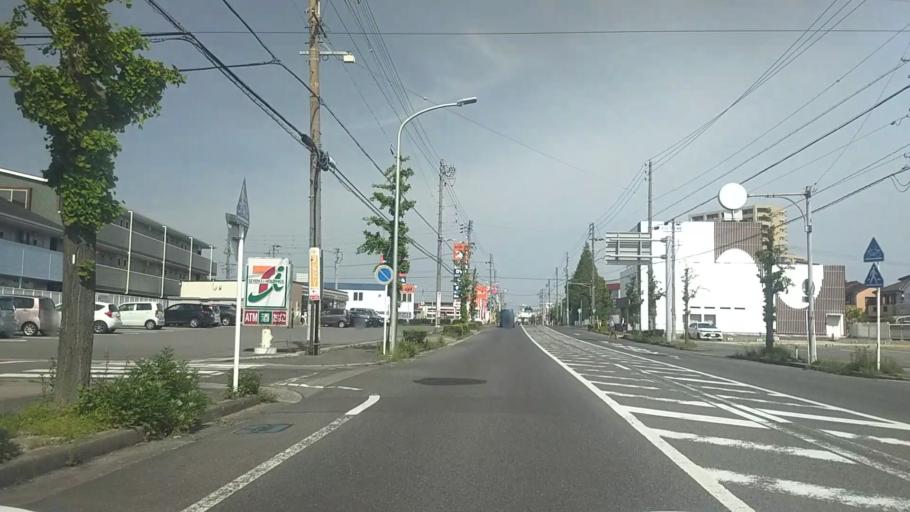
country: JP
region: Aichi
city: Anjo
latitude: 34.9544
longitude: 137.0783
